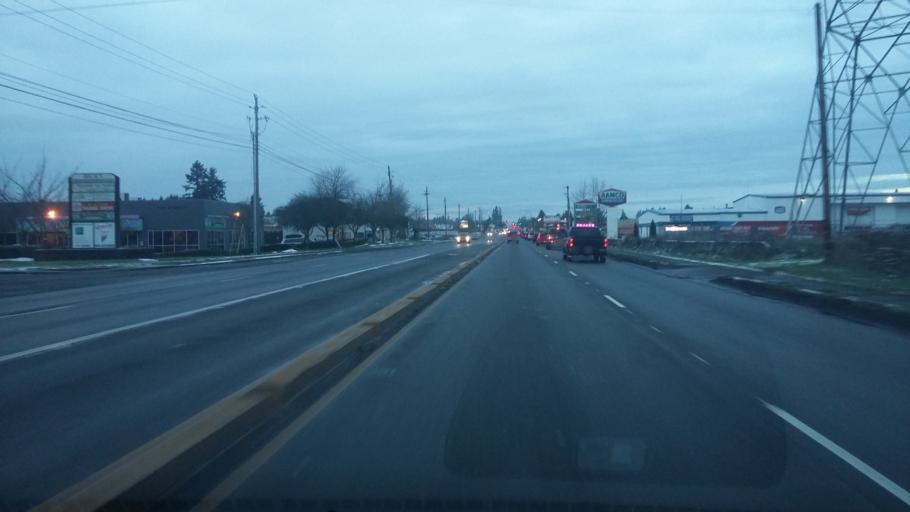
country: US
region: Washington
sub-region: Clark County
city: Orchards
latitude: 45.6703
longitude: -122.5525
